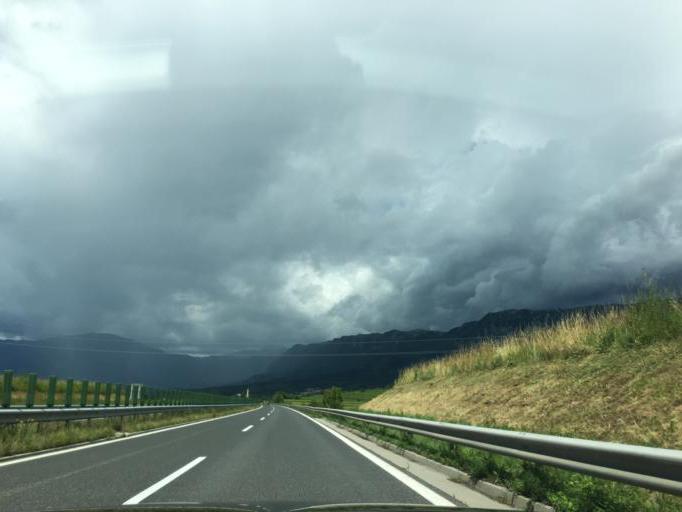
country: SI
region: Vipava
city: Vipava
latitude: 45.8457
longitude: 13.9502
